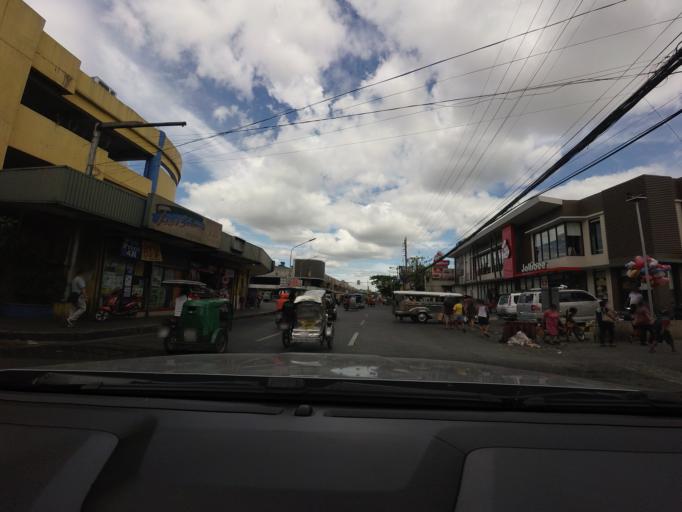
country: PH
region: Calabarzon
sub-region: Province of Rizal
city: Pateros
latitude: 14.5582
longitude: 121.0826
